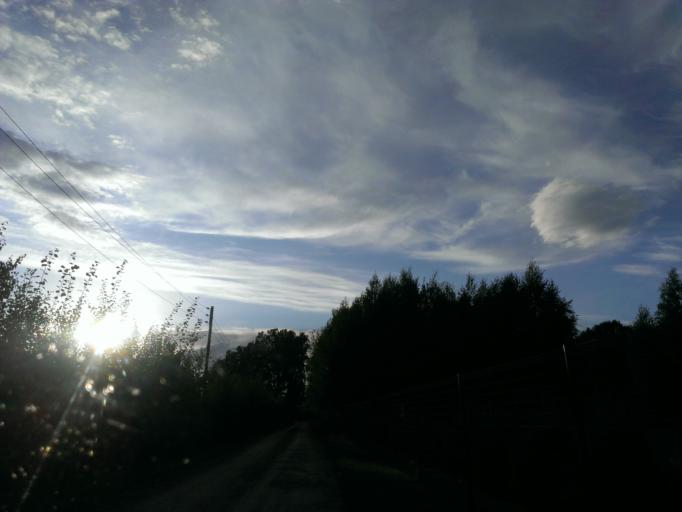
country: LV
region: Ikskile
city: Ikskile
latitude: 56.8354
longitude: 24.5212
